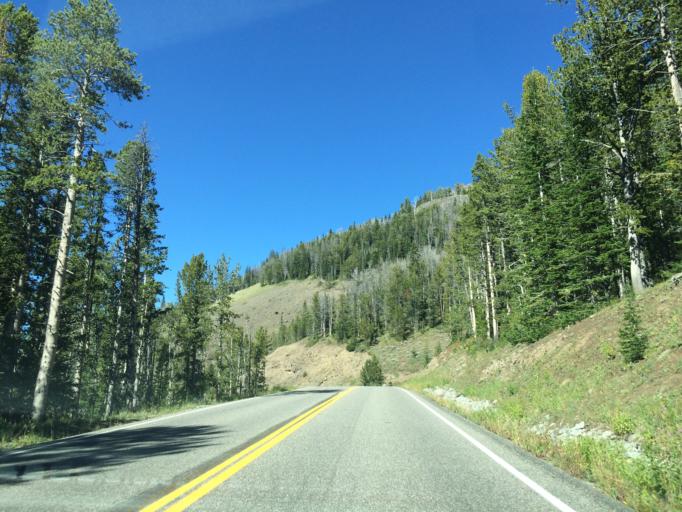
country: US
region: Montana
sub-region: Gallatin County
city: West Yellowstone
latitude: 44.7943
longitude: -110.4449
